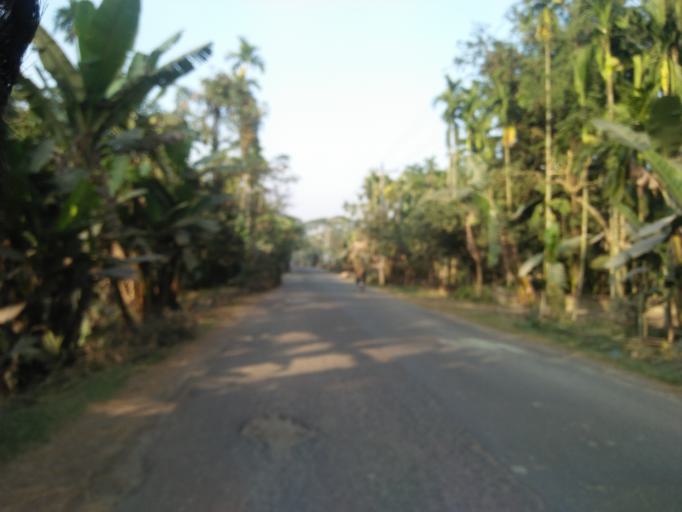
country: BD
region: Barisal
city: Bhola
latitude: 22.7410
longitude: 90.6341
